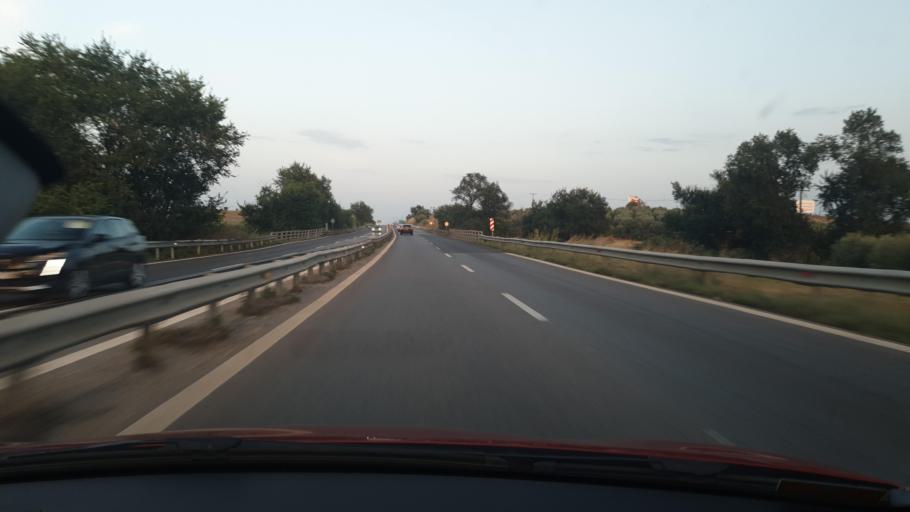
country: GR
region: Central Macedonia
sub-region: Nomos Chalkidikis
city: Nea Flogita
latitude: 40.2647
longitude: 23.2382
